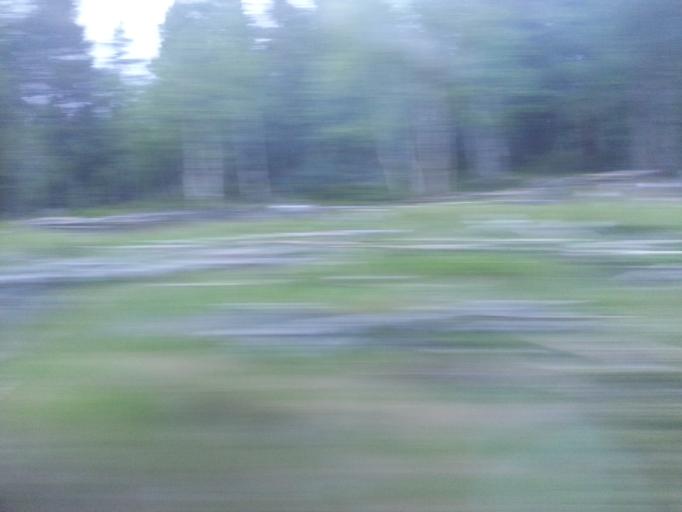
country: NO
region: Oppland
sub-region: Dovre
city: Dombas
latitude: 62.1109
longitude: 9.0946
